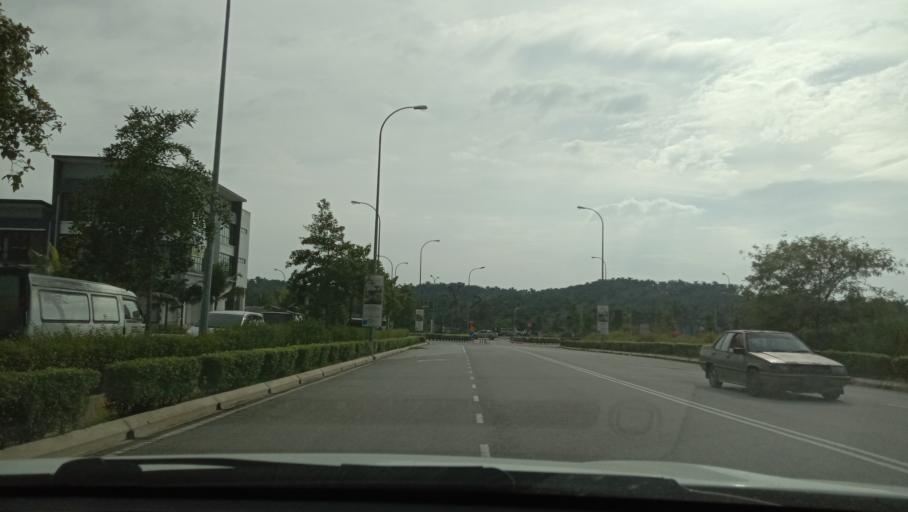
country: MY
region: Selangor
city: Ladang Seri Kundang
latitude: 3.2437
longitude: 101.4749
